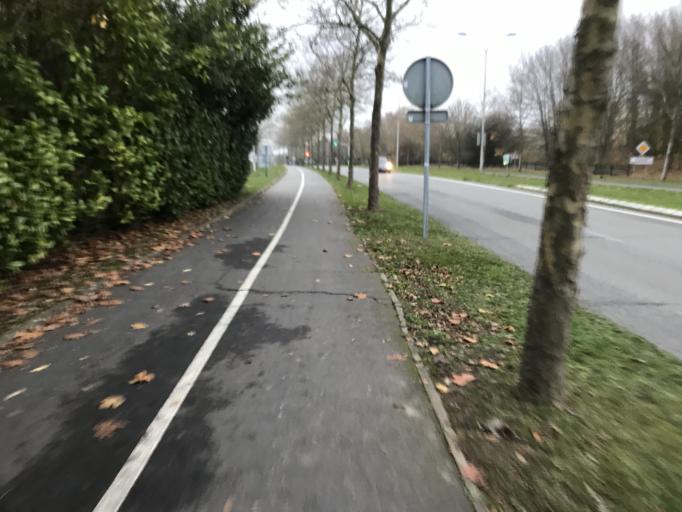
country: FR
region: Ile-de-France
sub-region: Departement des Yvelines
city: Saint-Quentin-en-Yvelines
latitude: 48.7669
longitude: 2.0096
